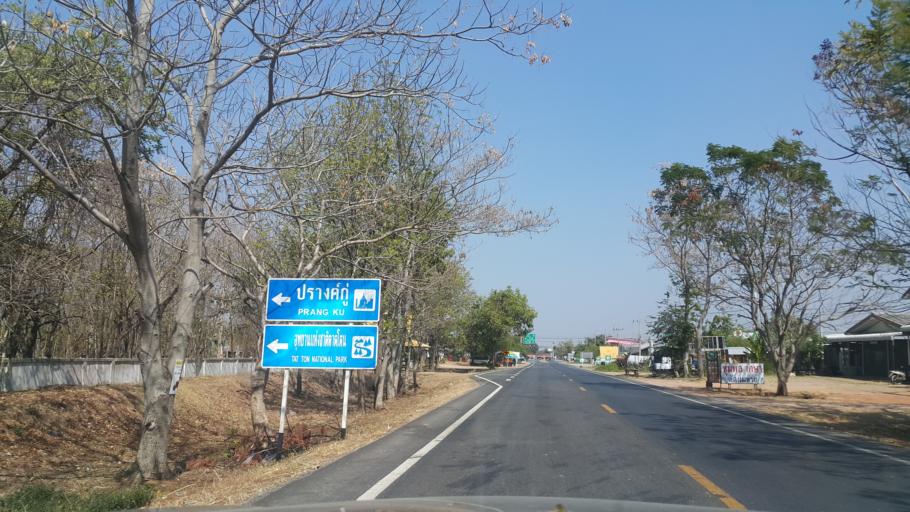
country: TH
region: Nakhon Ratchasima
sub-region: Amphoe Kaeng Sanam Nang
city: Kaeng Sanam Nang
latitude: 15.6875
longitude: 102.3301
